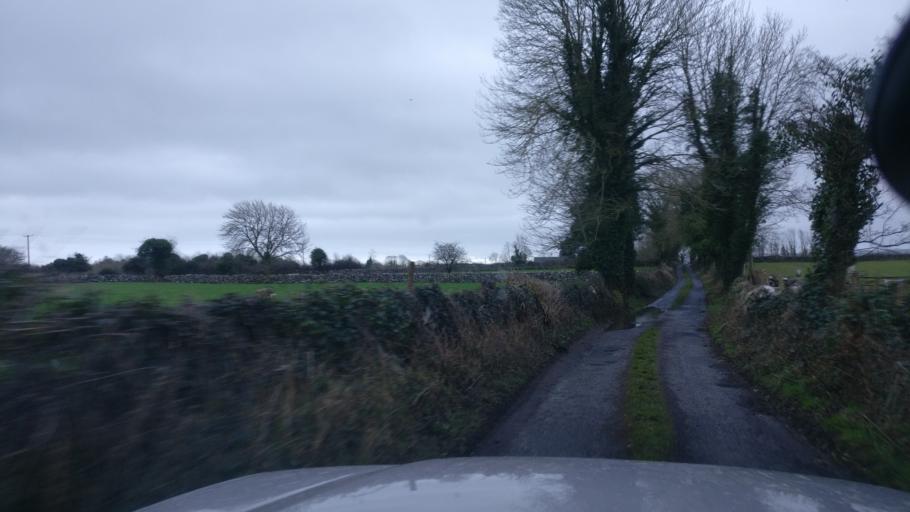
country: IE
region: Connaught
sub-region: County Galway
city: Loughrea
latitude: 53.1997
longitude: -8.6422
